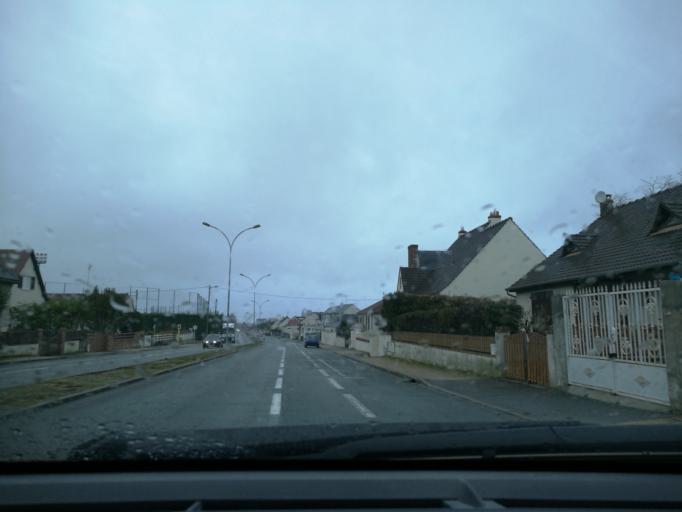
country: FR
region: Centre
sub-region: Departement du Loiret
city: Fleury-les-Aubrais
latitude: 47.9330
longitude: 1.9267
